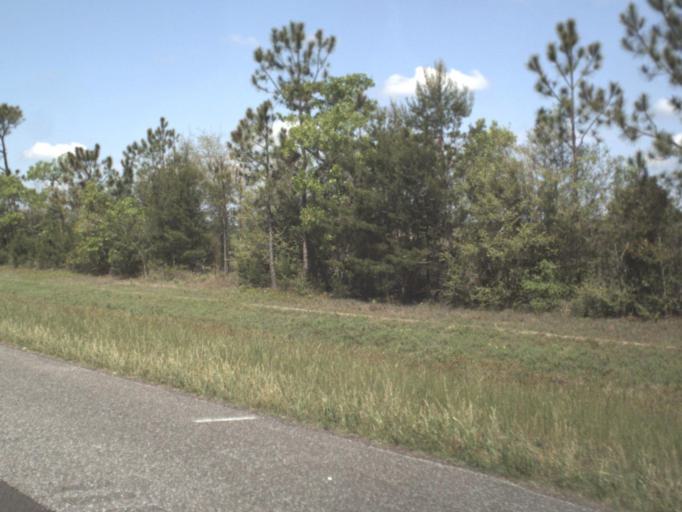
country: US
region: Florida
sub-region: Santa Rosa County
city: East Milton
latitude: 30.6739
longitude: -86.8353
